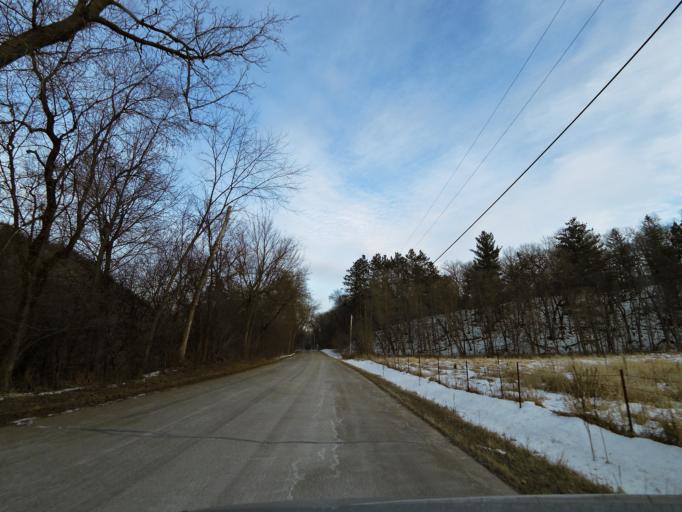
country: US
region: Minnesota
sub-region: Washington County
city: Afton
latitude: 44.9126
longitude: -92.8240
